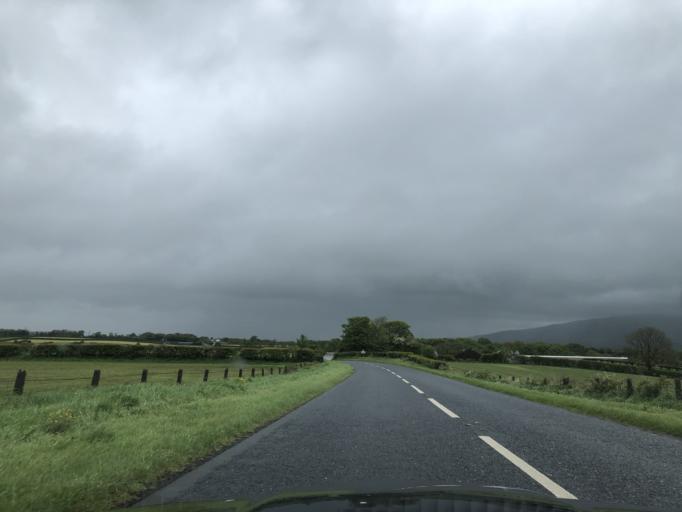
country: GB
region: Northern Ireland
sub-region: Moyle District
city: Ballycastle
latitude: 55.1706
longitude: -6.3480
